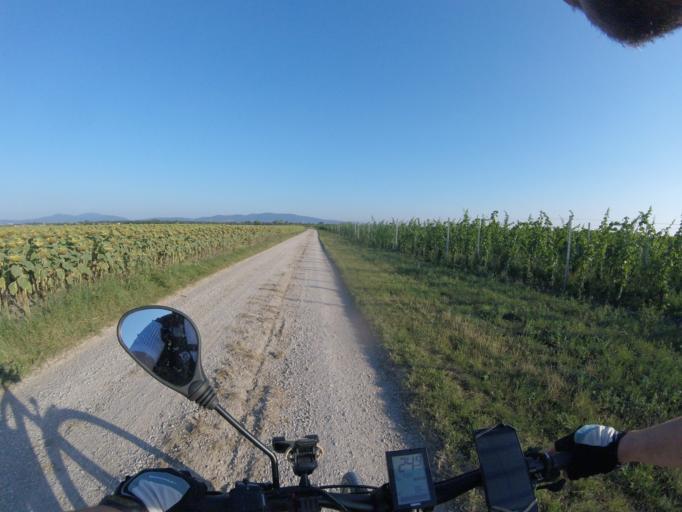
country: AT
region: Lower Austria
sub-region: Politischer Bezirk Baden
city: Trumau
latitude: 47.9821
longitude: 16.3553
